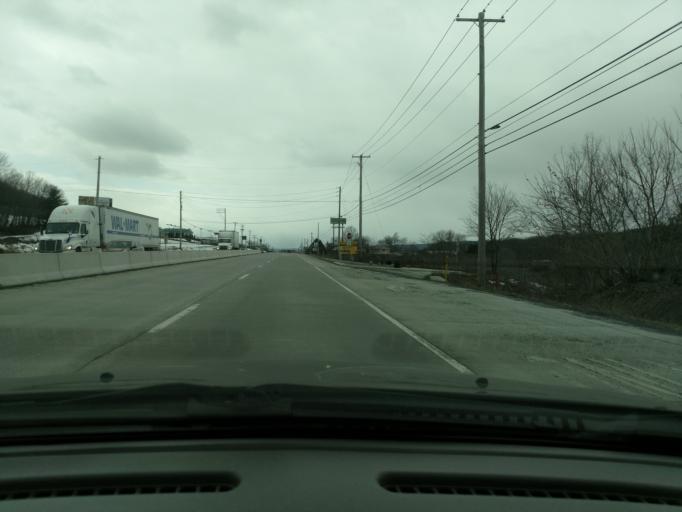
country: US
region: Pennsylvania
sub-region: Schuylkill County
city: Orwigsburg
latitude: 40.6398
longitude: -76.0832
